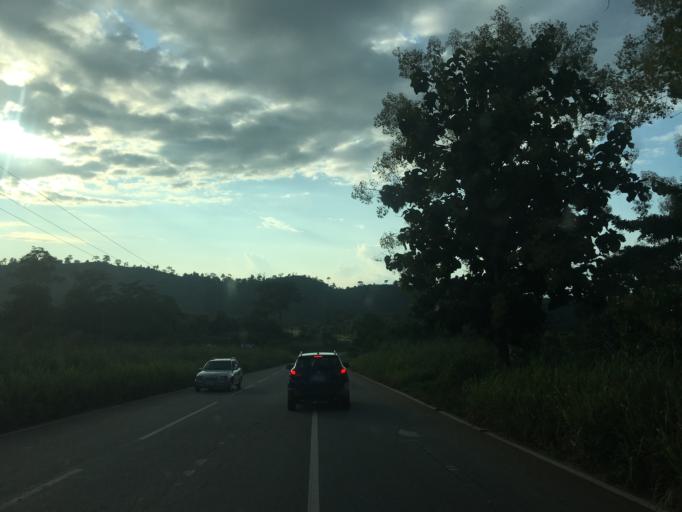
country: GH
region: Western
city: Bibiani
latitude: 6.4889
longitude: -2.3355
